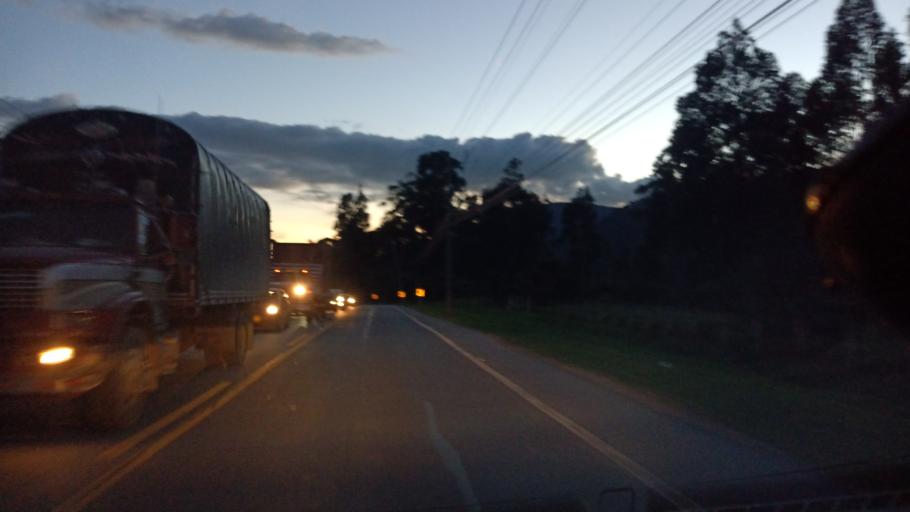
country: CO
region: Cundinamarca
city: Cota
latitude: 4.8383
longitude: -74.0859
